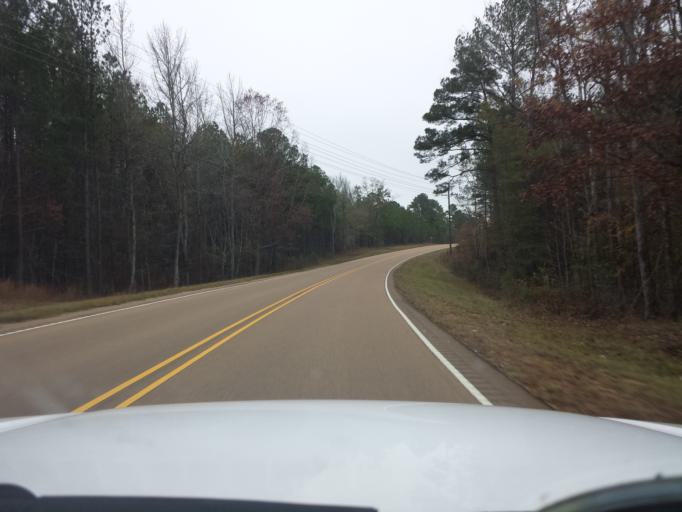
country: US
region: Mississippi
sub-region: Rankin County
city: Brandon
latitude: 32.4347
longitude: -89.9465
